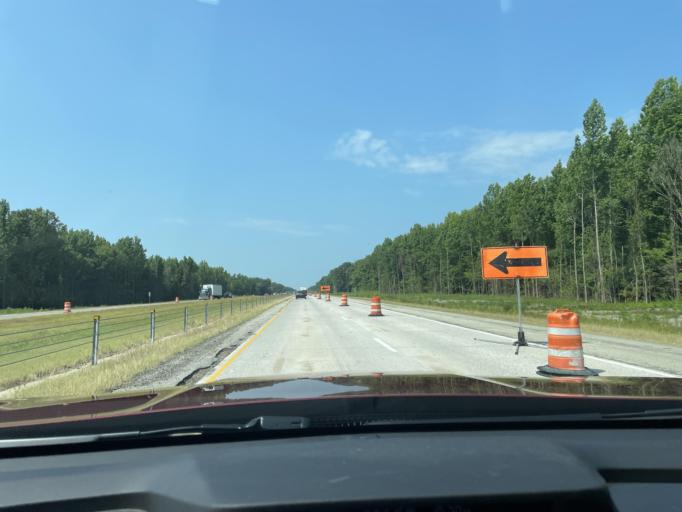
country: US
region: Arkansas
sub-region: White County
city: Searcy
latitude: 35.1831
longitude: -91.7561
